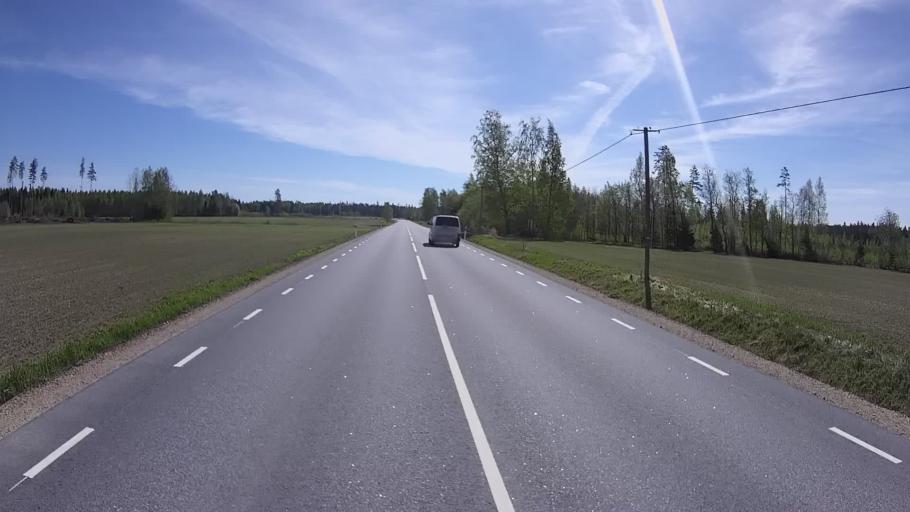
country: EE
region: Polvamaa
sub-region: Raepina vald
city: Rapina
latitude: 57.9795
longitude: 27.2816
